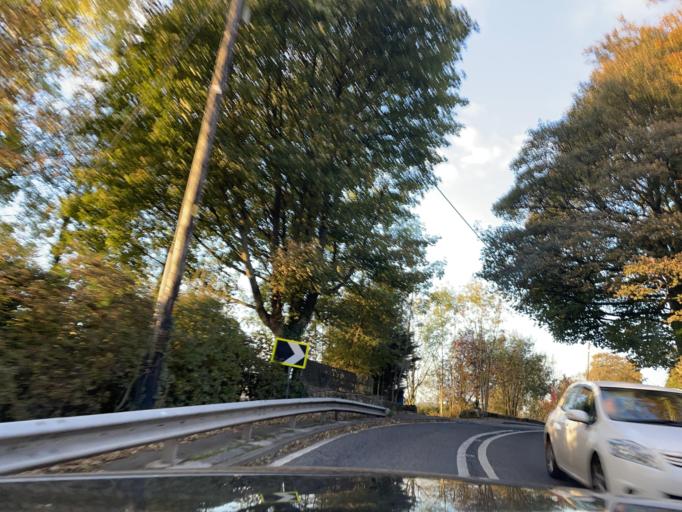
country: GB
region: England
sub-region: Borough of Stockport
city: Marple
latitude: 53.4204
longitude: -2.0308
